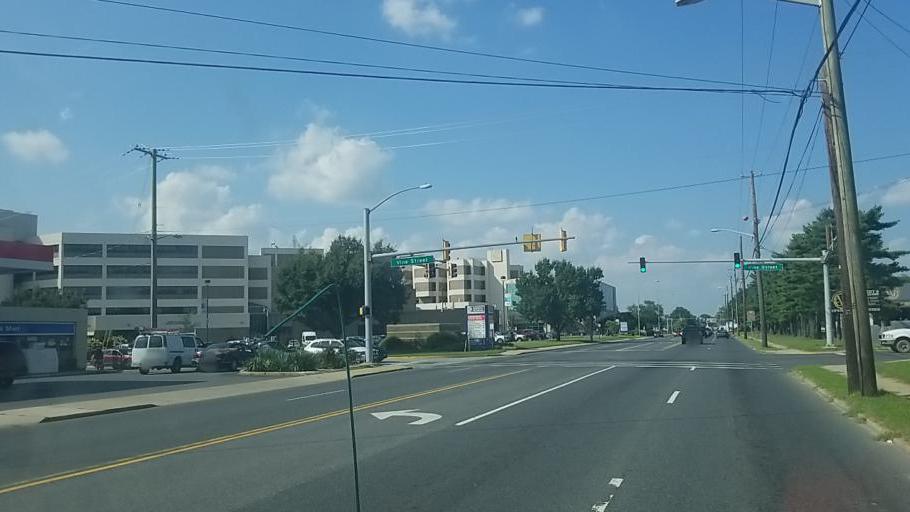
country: US
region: Maryland
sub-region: Wicomico County
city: Salisbury
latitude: 38.3603
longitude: -75.5971
